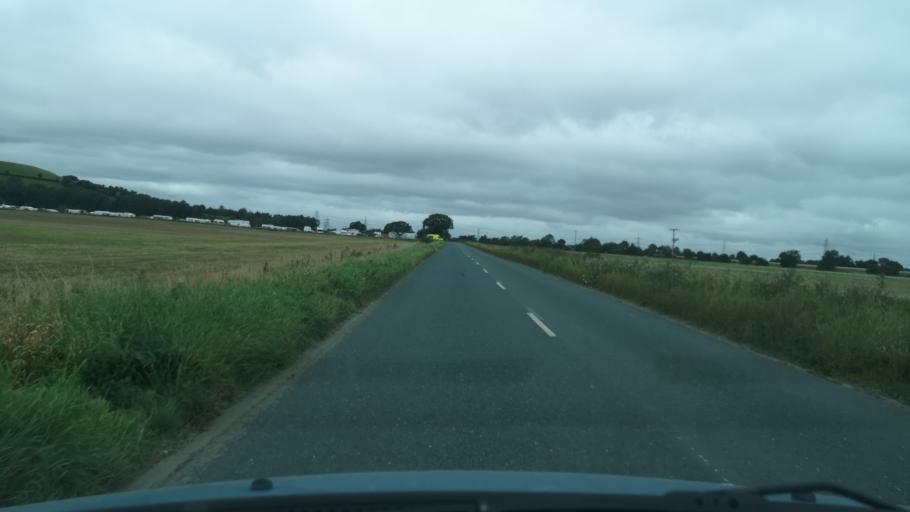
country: GB
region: England
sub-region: Doncaster
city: Norton
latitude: 53.6916
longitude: -1.1693
